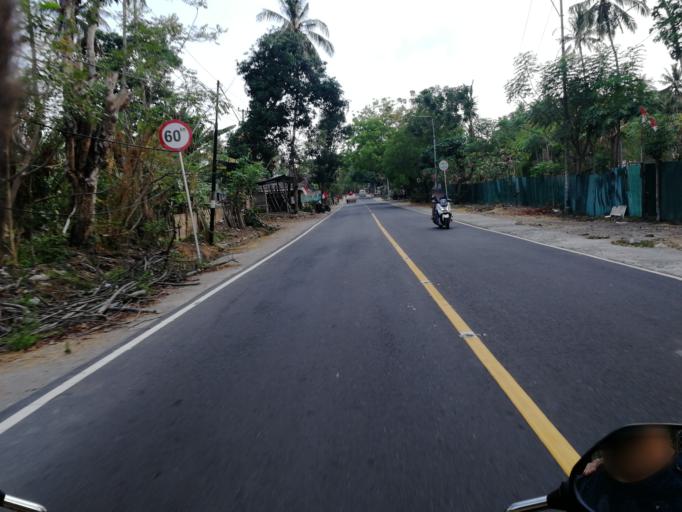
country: ID
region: West Nusa Tenggara
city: Karangsubagan
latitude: -8.4845
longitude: 116.0384
